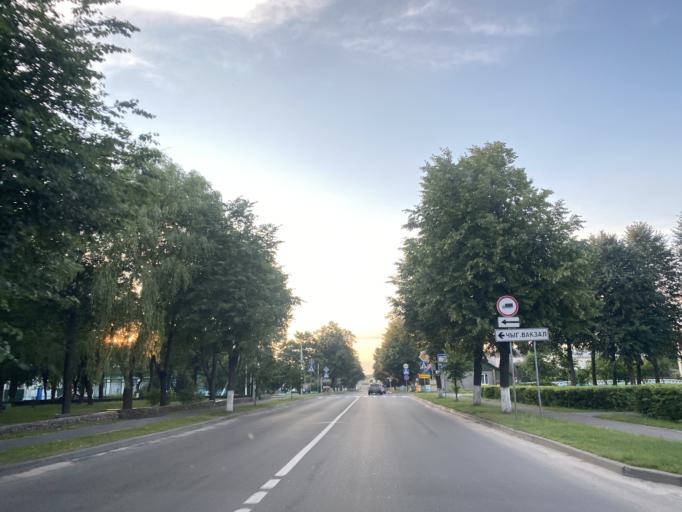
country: BY
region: Brest
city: Ivatsevichy
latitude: 52.7125
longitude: 25.3504
